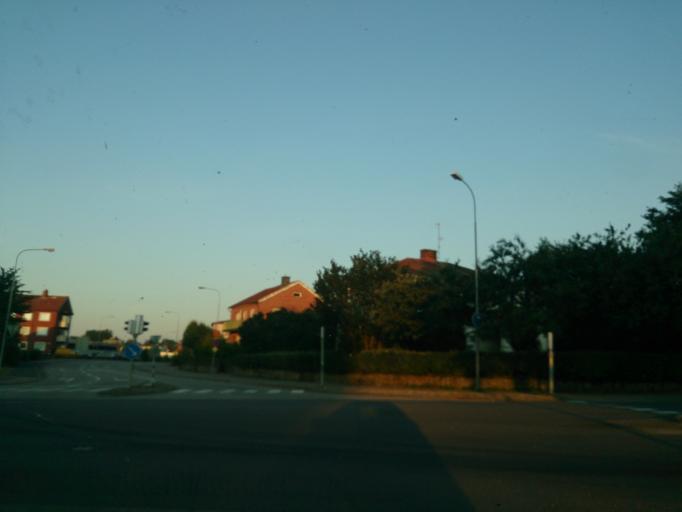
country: SE
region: Kronoberg
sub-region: Alvesta Kommun
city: Alvesta
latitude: 56.9028
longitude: 14.5552
